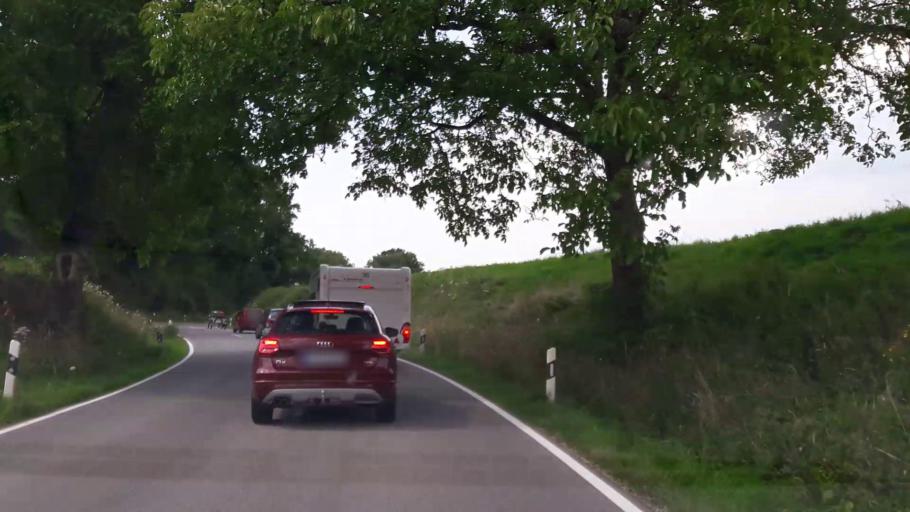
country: DE
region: Bavaria
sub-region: Upper Bavaria
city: Teisendorf
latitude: 47.8326
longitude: 12.8359
